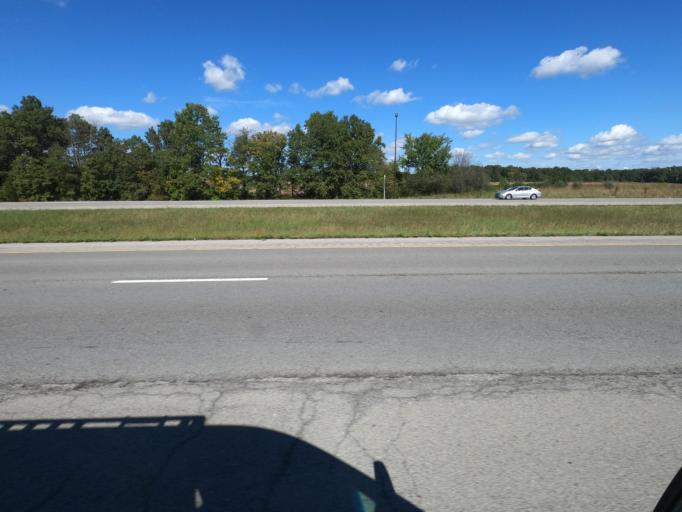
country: US
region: Illinois
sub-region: Jefferson County
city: Mount Vernon
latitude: 38.3615
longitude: -89.0302
